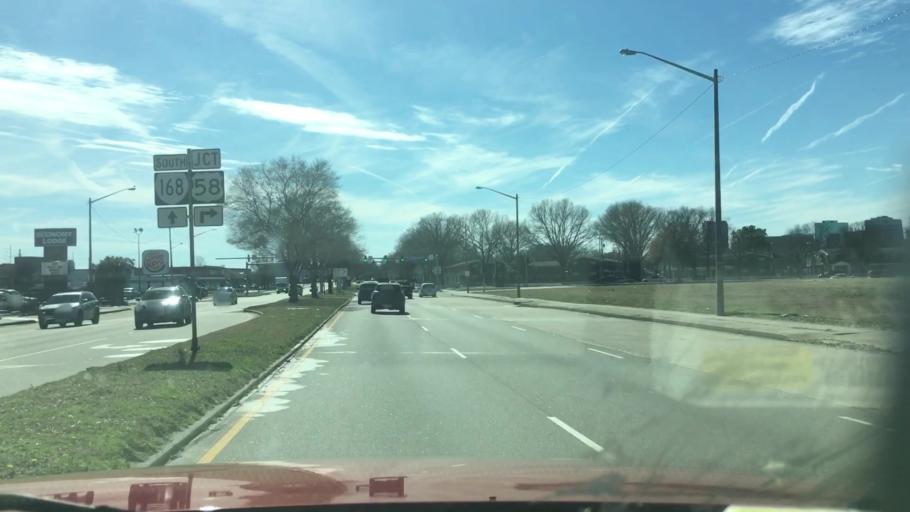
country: US
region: Virginia
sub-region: City of Norfolk
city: Norfolk
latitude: 36.8559
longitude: -76.2739
